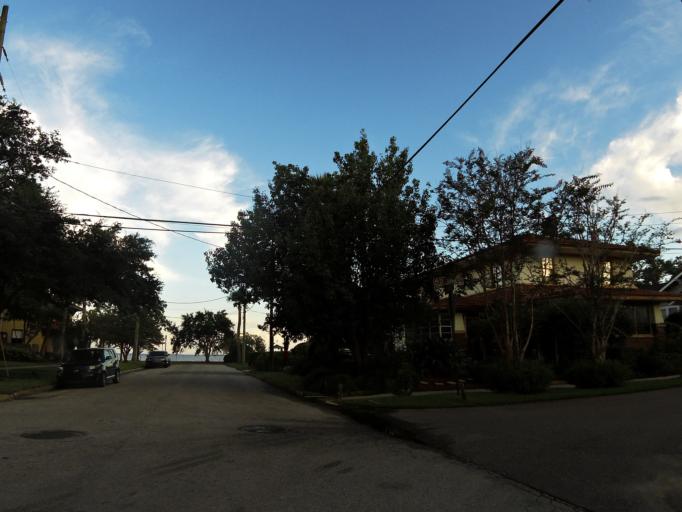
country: US
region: Florida
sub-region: Duval County
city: Jacksonville
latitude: 30.3098
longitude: -81.6839
